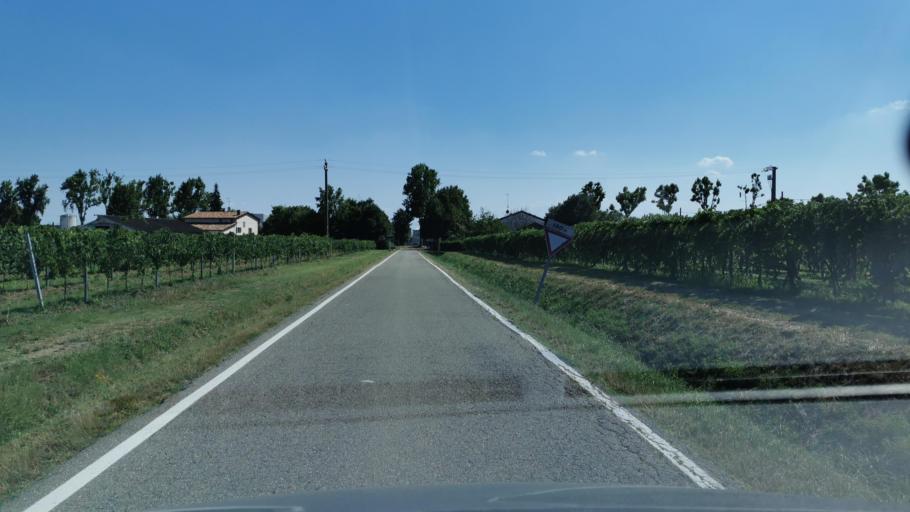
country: IT
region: Emilia-Romagna
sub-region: Provincia di Modena
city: Limidi
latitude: 44.7678
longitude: 10.9167
